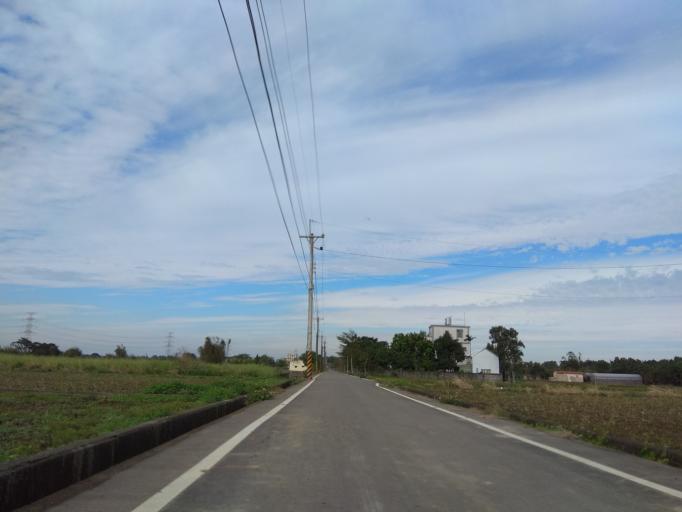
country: TW
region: Taiwan
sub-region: Hsinchu
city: Zhubei
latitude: 24.9517
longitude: 121.1106
